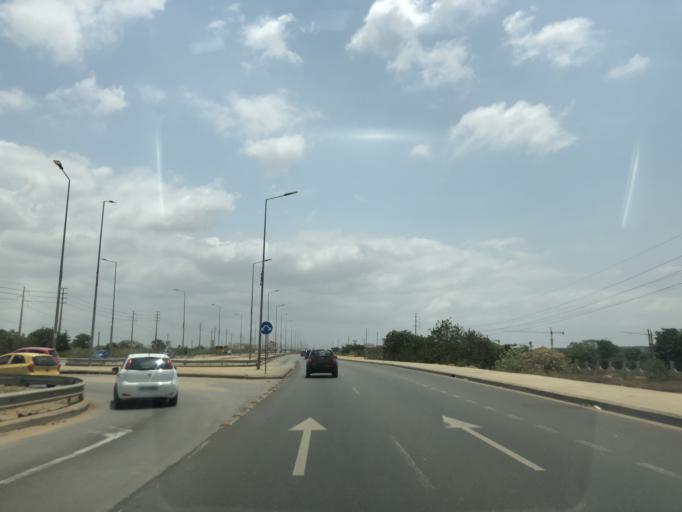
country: AO
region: Luanda
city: Luanda
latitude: -8.9469
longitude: 13.2600
